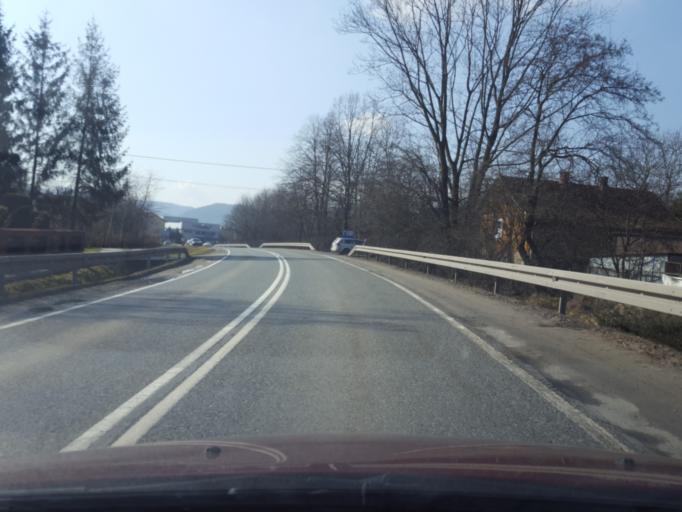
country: PL
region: Lesser Poland Voivodeship
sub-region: Powiat brzeski
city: Czchow
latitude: 49.8481
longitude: 20.6859
